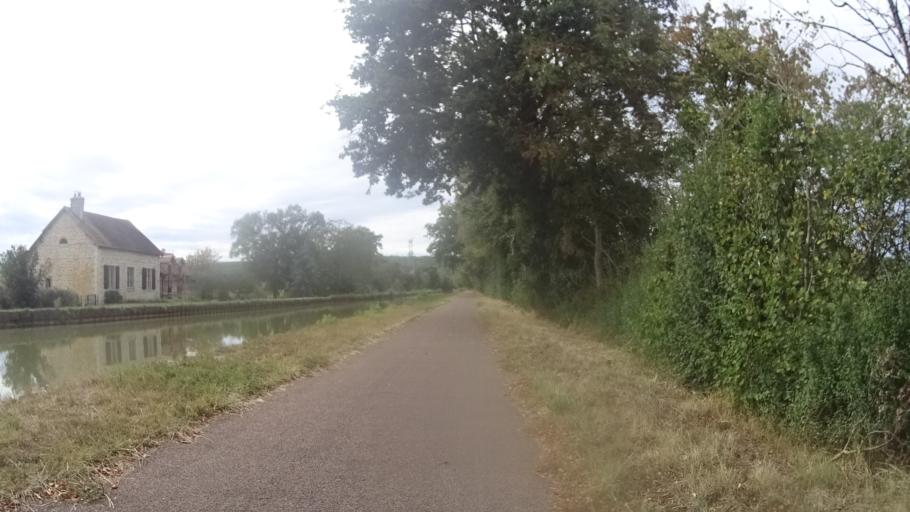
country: FR
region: Bourgogne
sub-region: Departement de la Nievre
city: Sermoise-sur-Loire
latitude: 46.9347
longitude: 3.2152
